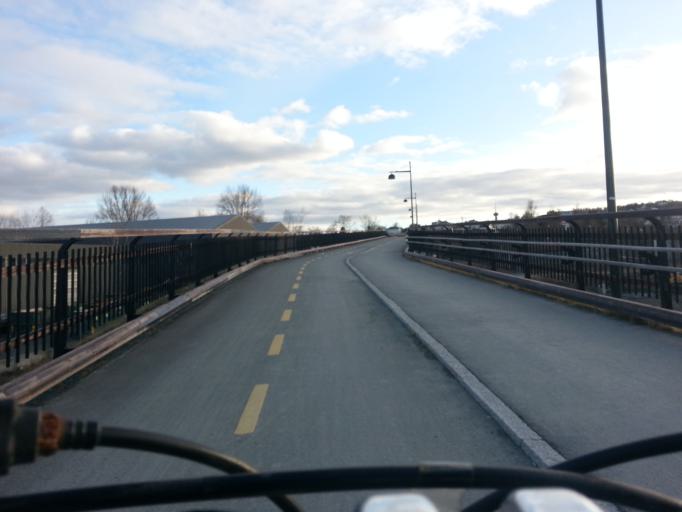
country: NO
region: Sor-Trondelag
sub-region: Trondheim
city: Trondheim
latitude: 63.4414
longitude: 10.4484
